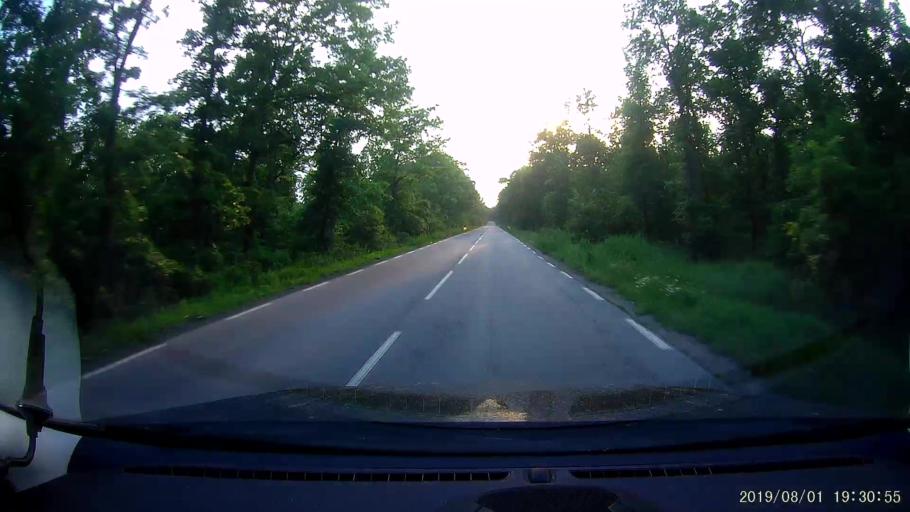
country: BG
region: Burgas
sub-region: Obshtina Sungurlare
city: Sungurlare
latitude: 42.8099
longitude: 26.8846
